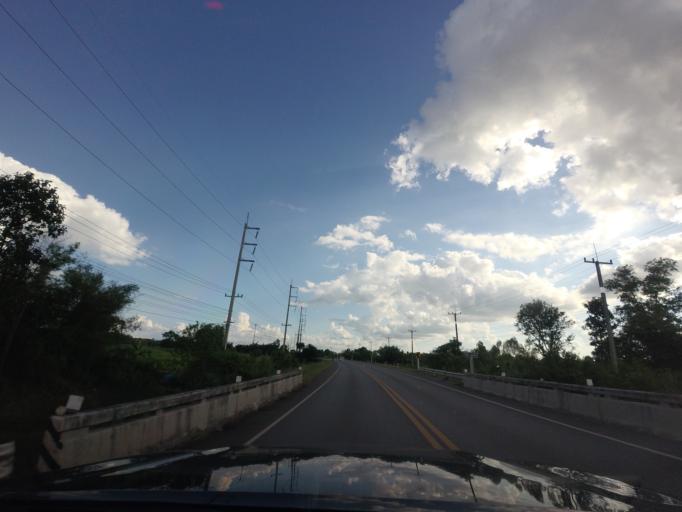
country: TH
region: Changwat Udon Thani
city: Thung Fon
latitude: 17.5136
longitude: 103.2036
